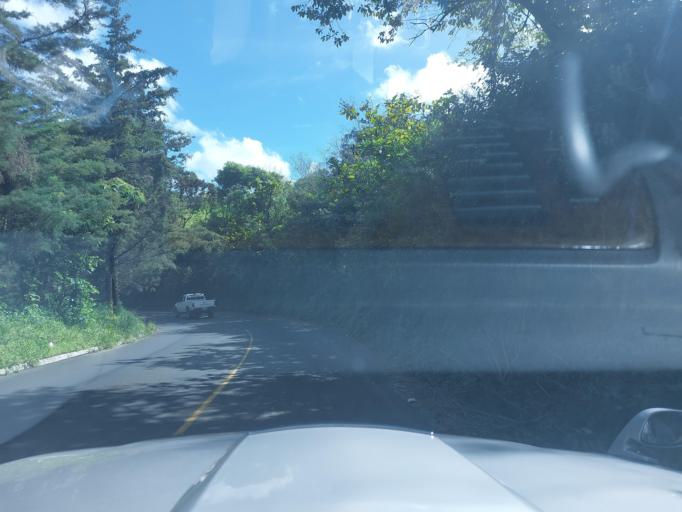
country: GT
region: Chimaltenango
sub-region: Municipio de Santa Cruz Balanya
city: Santa Cruz Balanya
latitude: 14.6808
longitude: -90.8952
